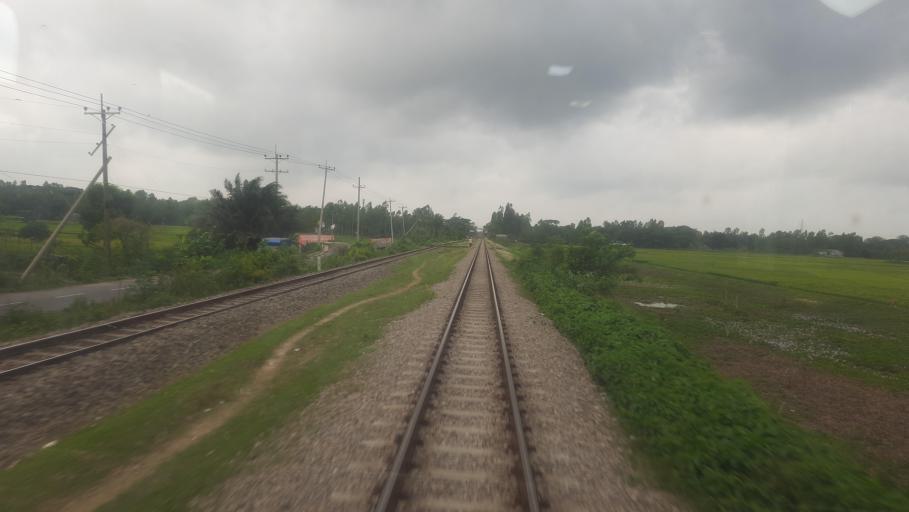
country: BD
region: Dhaka
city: Narsingdi
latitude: 23.9727
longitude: 90.8294
